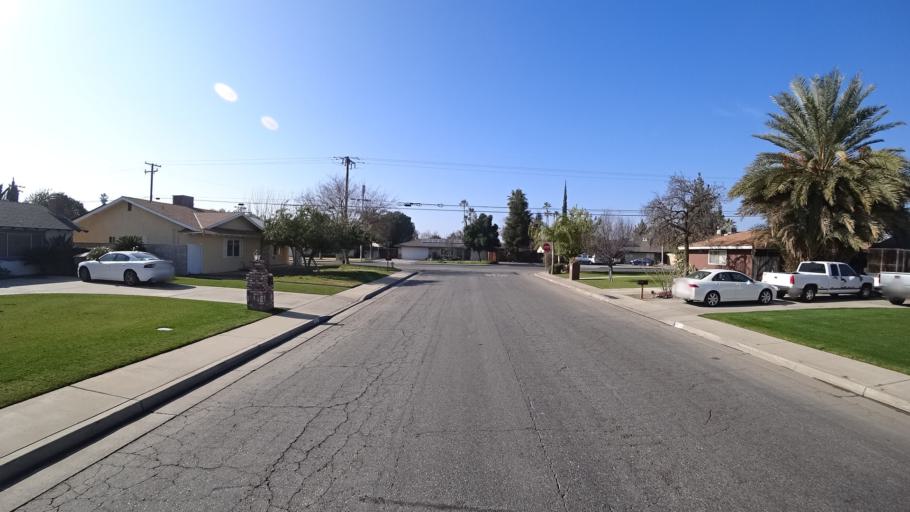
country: US
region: California
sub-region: Kern County
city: Bakersfield
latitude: 35.3370
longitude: -119.0430
